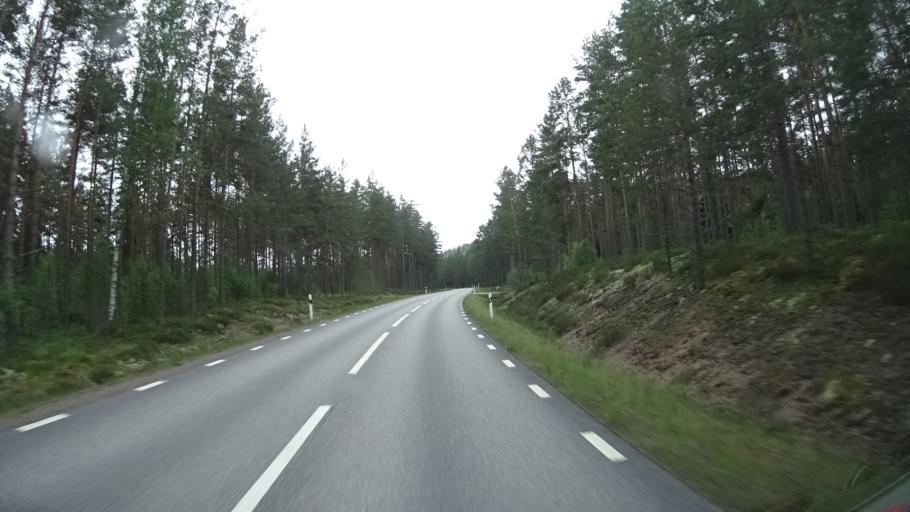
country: SE
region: Joenkoeping
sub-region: Eksjo Kommun
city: Mariannelund
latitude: 57.5681
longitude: 15.7047
